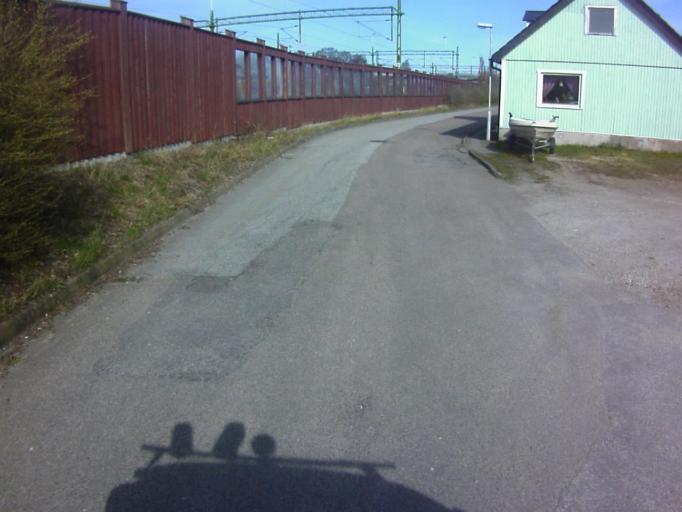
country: SE
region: Skane
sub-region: Kavlinge Kommun
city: Kaevlinge
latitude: 55.7953
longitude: 13.1117
